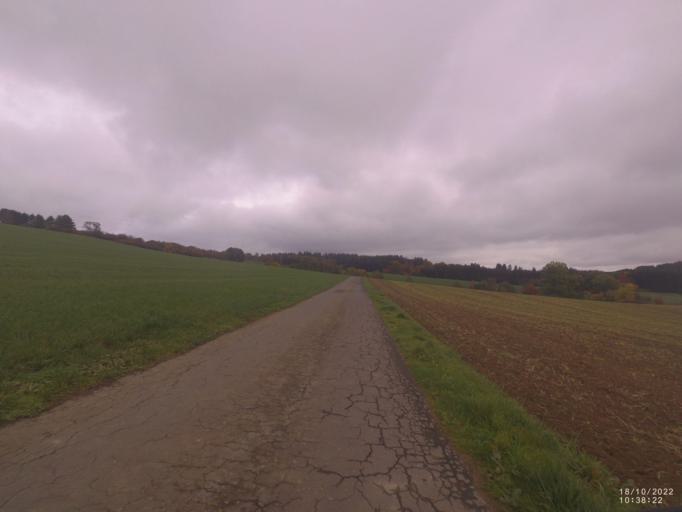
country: DE
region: Rheinland-Pfalz
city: Darscheid
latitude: 50.2187
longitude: 6.8978
